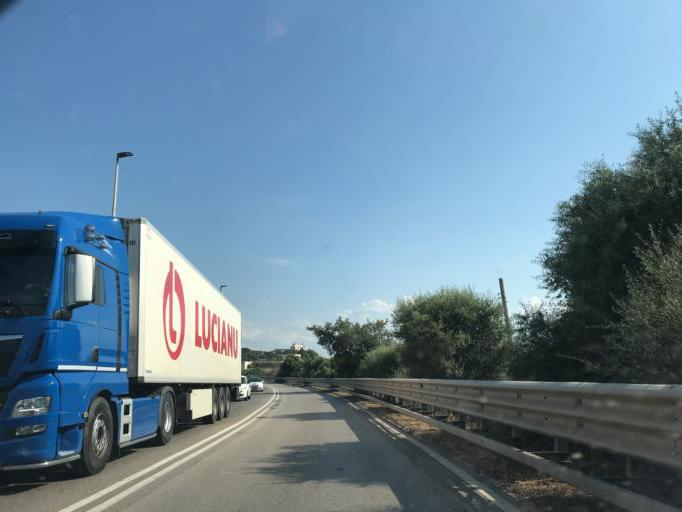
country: IT
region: Sardinia
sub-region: Provincia di Olbia-Tempio
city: Olbia
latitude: 40.9145
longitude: 9.5016
